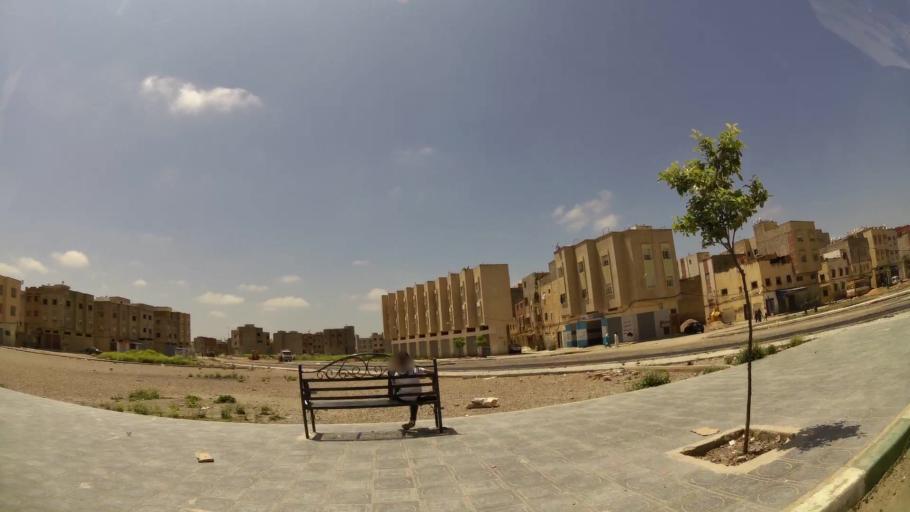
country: MA
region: Fes-Boulemane
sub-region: Fes
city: Fes
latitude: 34.0335
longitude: -5.0475
